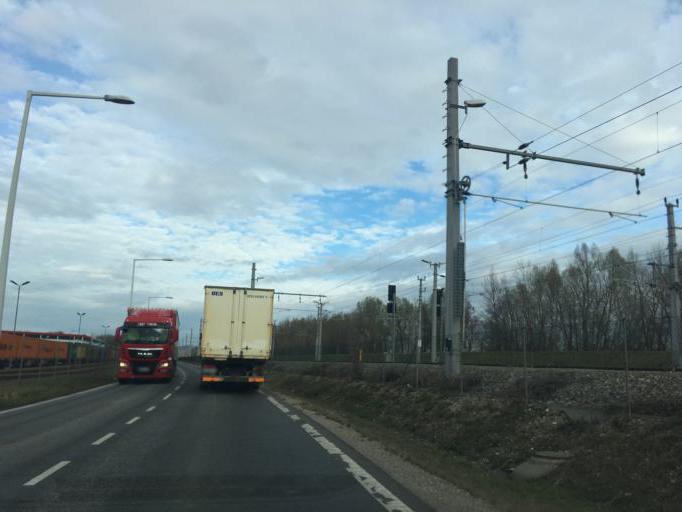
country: AT
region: Lower Austria
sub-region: Politischer Bezirk Wien-Umgebung
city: Schwechat
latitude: 48.1848
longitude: 16.4634
